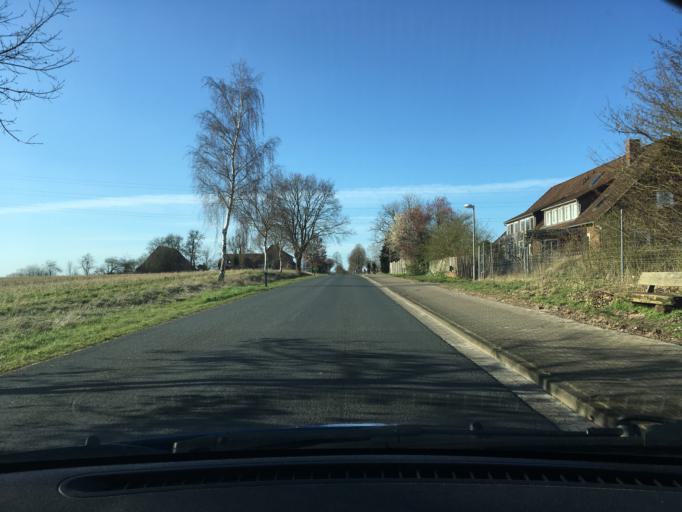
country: DE
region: Lower Saxony
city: Embsen
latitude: 53.2139
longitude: 10.3670
